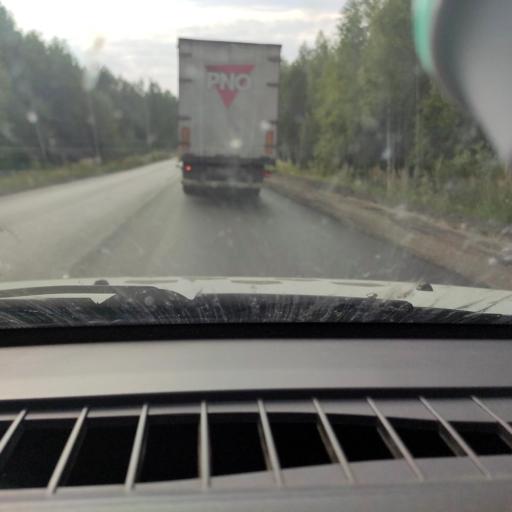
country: RU
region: Kirov
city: Chernaya Kholunitsa
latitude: 58.8774
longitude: 51.4674
